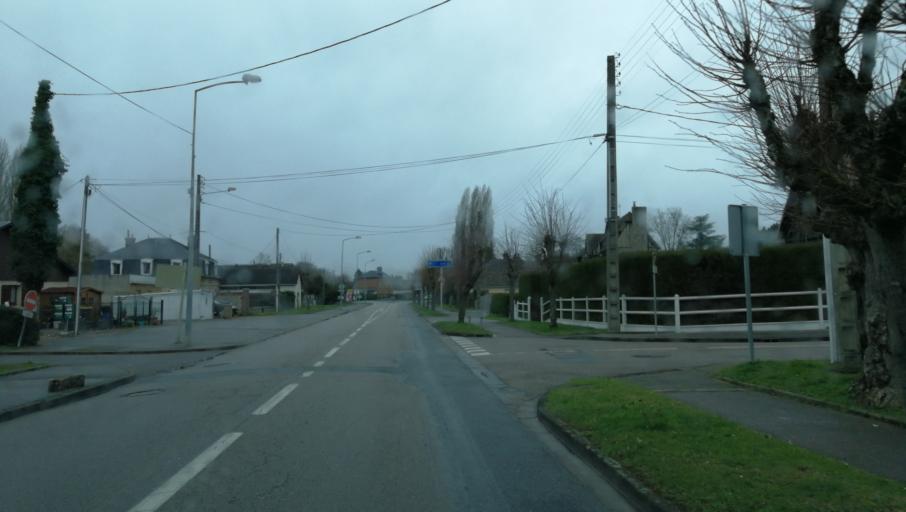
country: FR
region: Haute-Normandie
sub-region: Departement de l'Eure
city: Brionne
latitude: 49.1917
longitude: 0.7217
